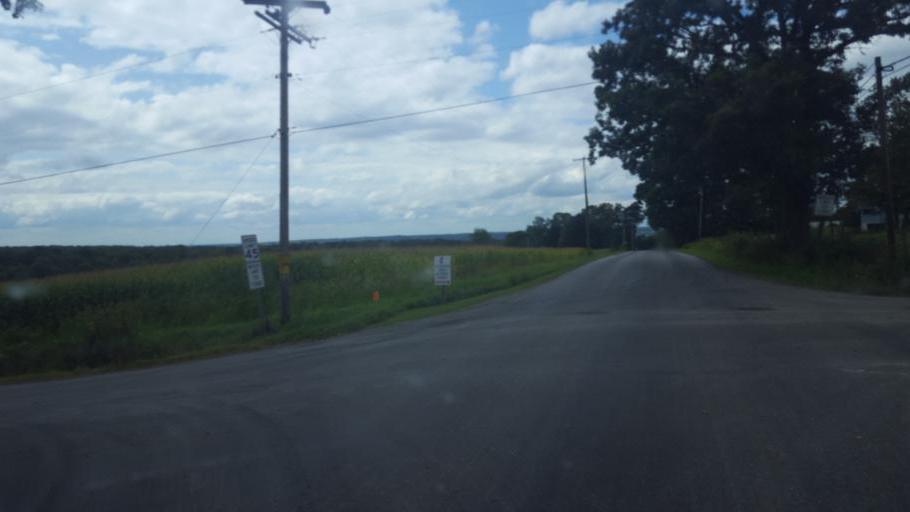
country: US
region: Pennsylvania
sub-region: Crawford County
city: Conneaut Lakeshore
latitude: 41.5039
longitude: -80.3078
